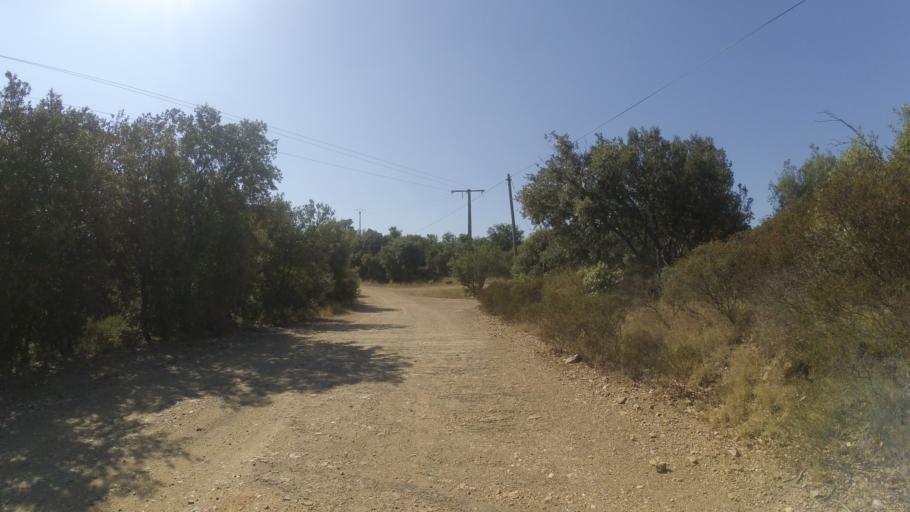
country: FR
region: Languedoc-Roussillon
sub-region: Departement des Pyrenees-Orientales
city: Millas
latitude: 42.6170
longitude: 2.6771
